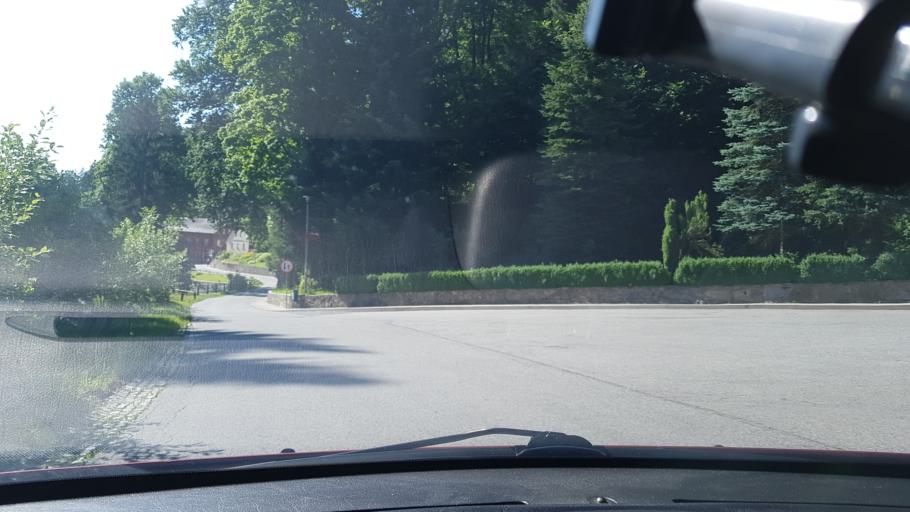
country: PL
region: Lower Silesian Voivodeship
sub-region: Powiat klodzki
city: Stronie Slaskie
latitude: 50.2279
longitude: 16.7677
